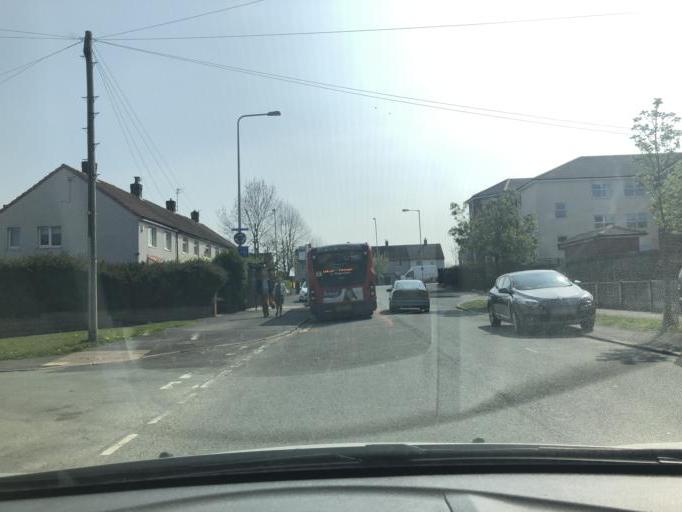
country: GB
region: England
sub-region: Borough of Stockport
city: Bredbury
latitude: 53.4291
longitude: -2.1297
